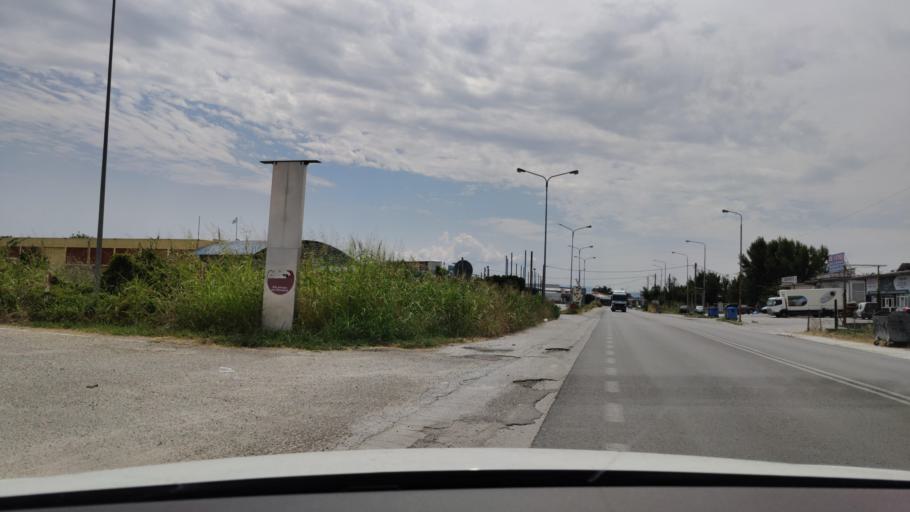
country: GR
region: Central Macedonia
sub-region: Nomos Serron
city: Serres
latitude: 41.0668
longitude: 23.5405
